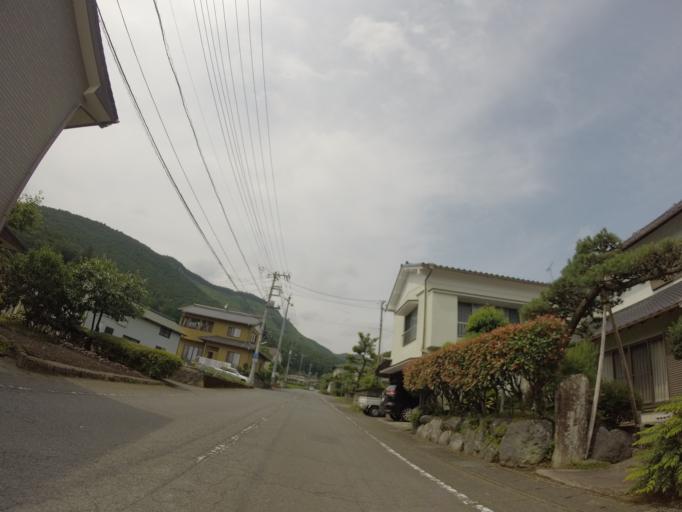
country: JP
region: Shizuoka
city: Fujinomiya
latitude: 35.2712
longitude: 138.5599
